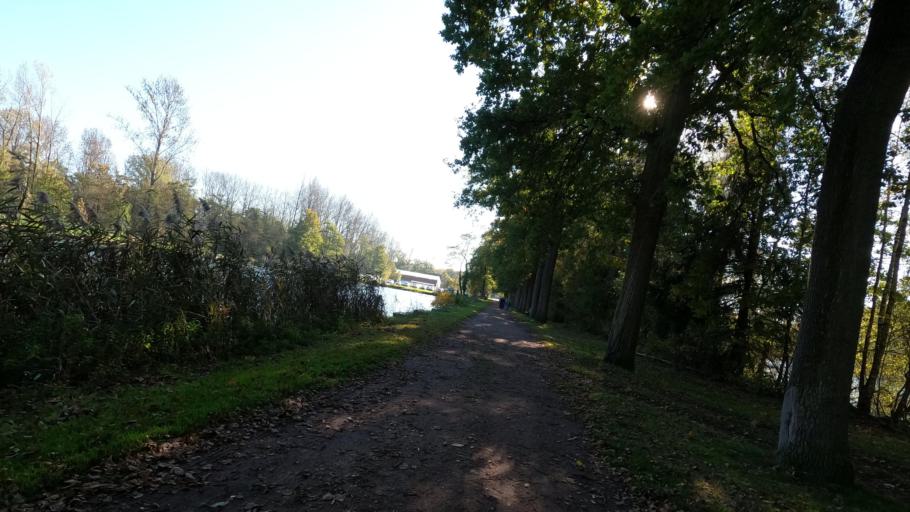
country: BE
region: Flanders
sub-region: Provincie Antwerpen
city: Merksplas
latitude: 51.3612
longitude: 4.8334
